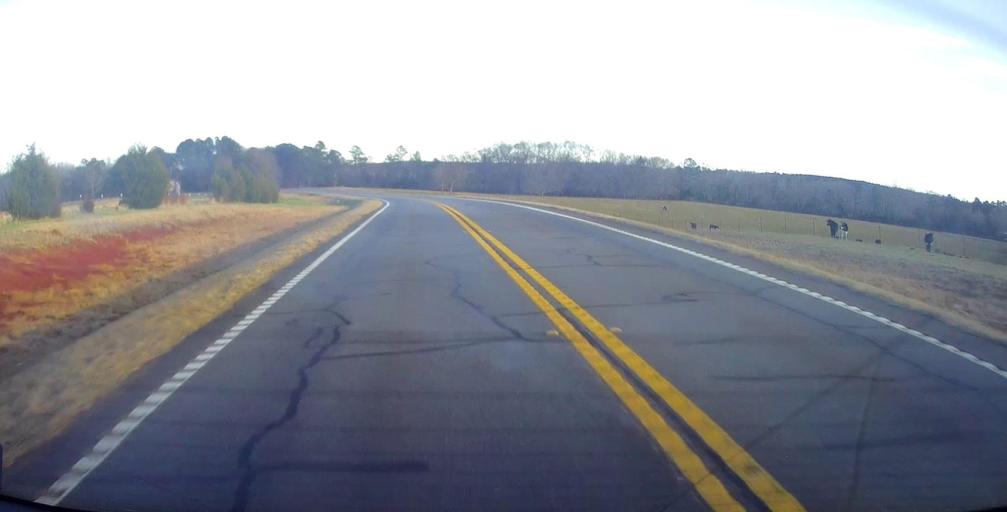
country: US
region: Georgia
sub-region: Talbot County
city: Talbotton
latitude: 32.7857
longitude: -84.5286
